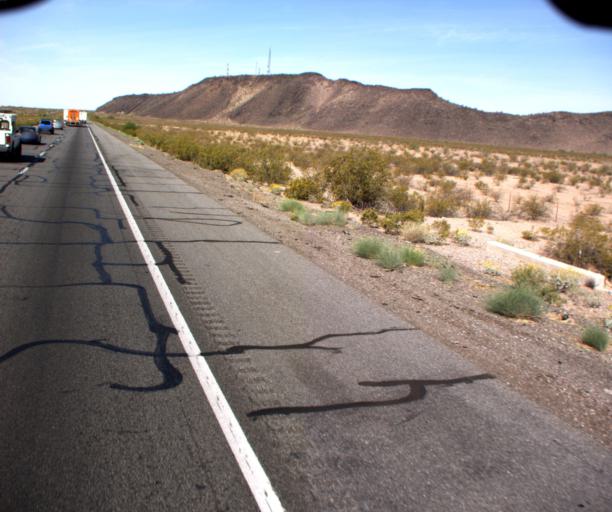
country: US
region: Arizona
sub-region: Maricopa County
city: Buckeye
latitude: 33.5248
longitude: -113.0929
